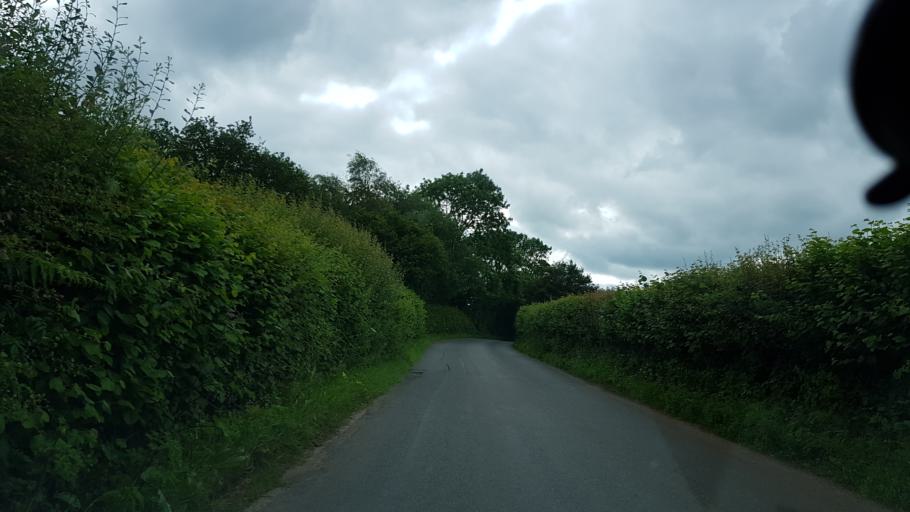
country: GB
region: England
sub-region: Herefordshire
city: Llancillo
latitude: 51.8960
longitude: -2.9344
